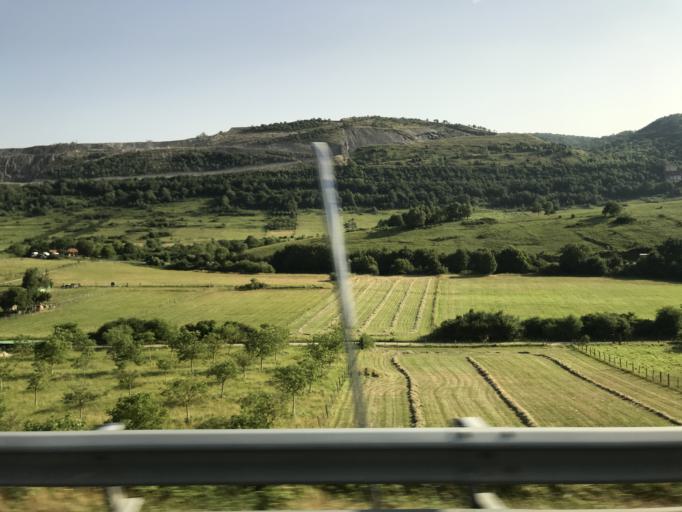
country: ES
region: Navarre
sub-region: Provincia de Navarra
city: Altsasu
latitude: 42.9157
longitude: -2.1892
